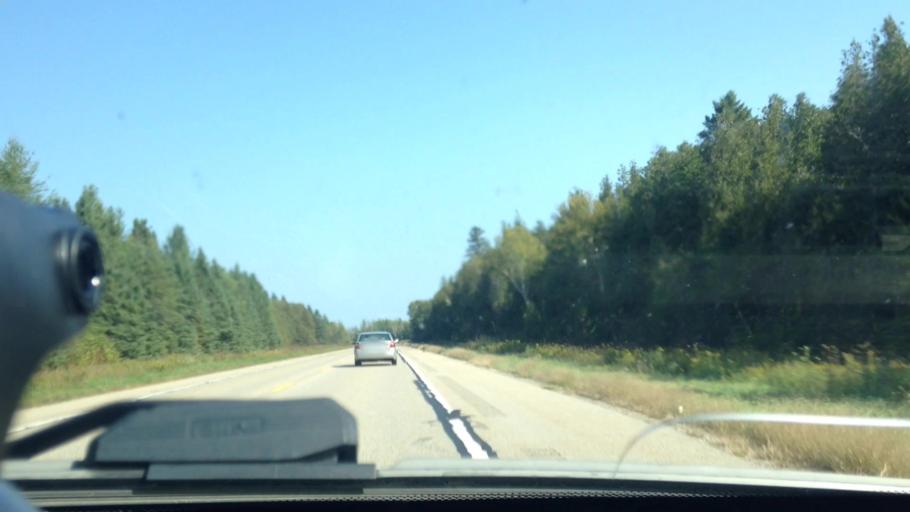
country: US
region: Michigan
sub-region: Luce County
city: Newberry
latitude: 46.3036
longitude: -85.2359
